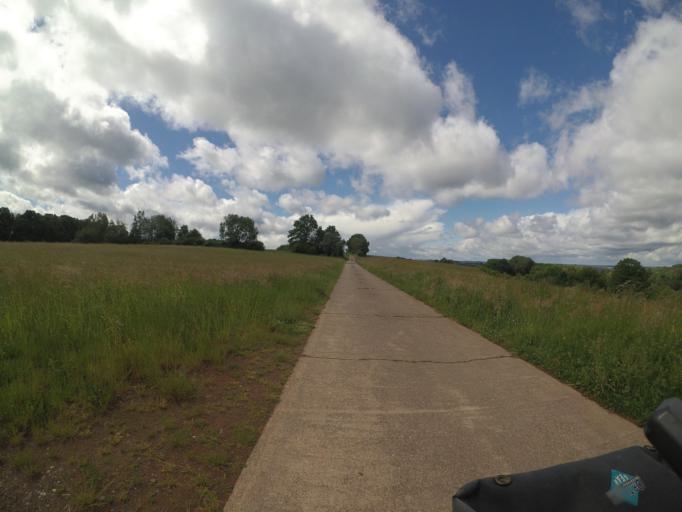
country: DE
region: Rheinland-Pfalz
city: Eppenbrunn
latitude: 49.1326
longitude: 7.5682
